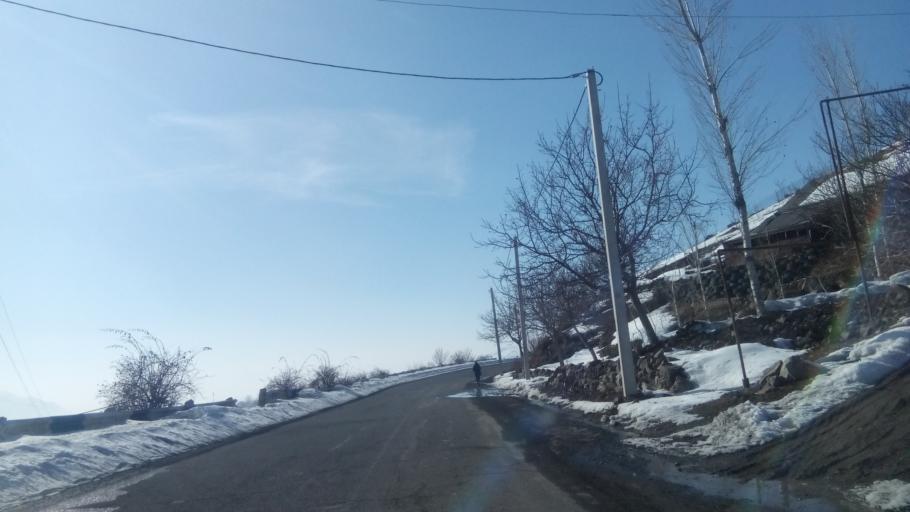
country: AM
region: Kotayk'i Marz
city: Goght'
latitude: 40.1399
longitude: 44.7935
